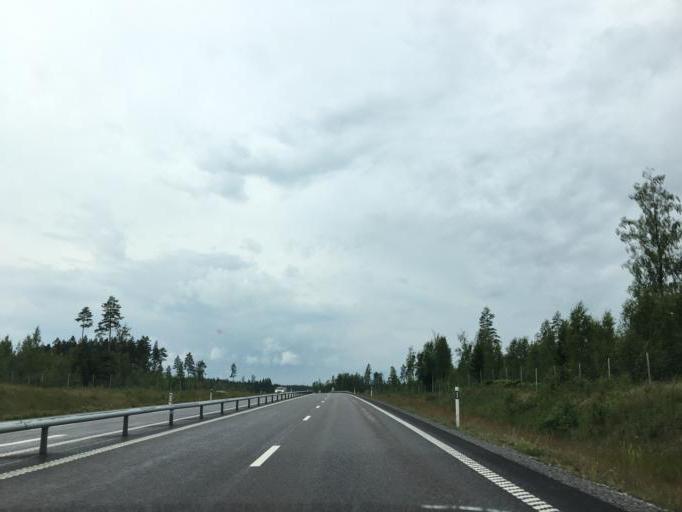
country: SE
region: Soedermanland
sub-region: Katrineholms Kommun
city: Katrineholm
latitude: 58.9533
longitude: 16.2208
